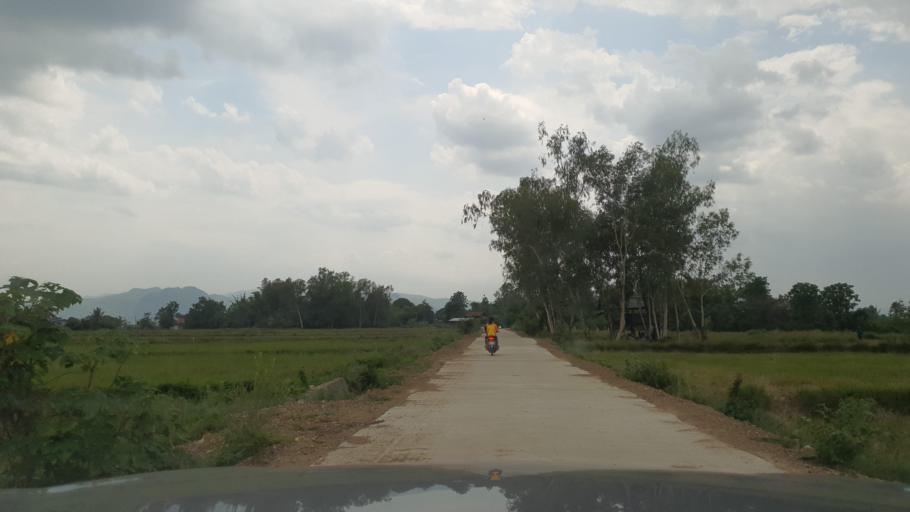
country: TH
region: Sukhothai
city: Thung Saliam
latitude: 17.3304
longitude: 99.4425
